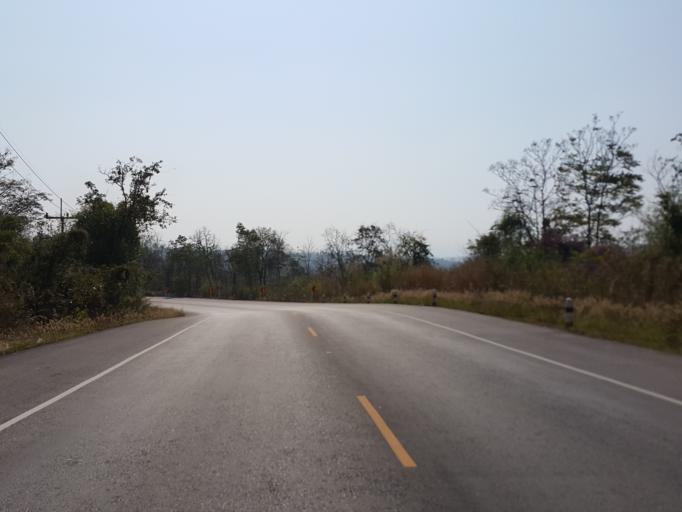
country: TH
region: Lampang
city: Mueang Pan
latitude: 18.8710
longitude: 99.5976
